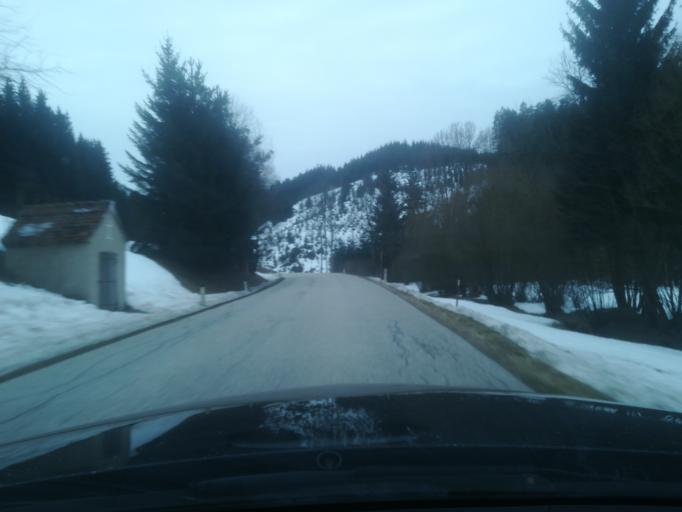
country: AT
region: Upper Austria
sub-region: Politischer Bezirk Perg
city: Perg
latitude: 48.3880
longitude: 14.6300
